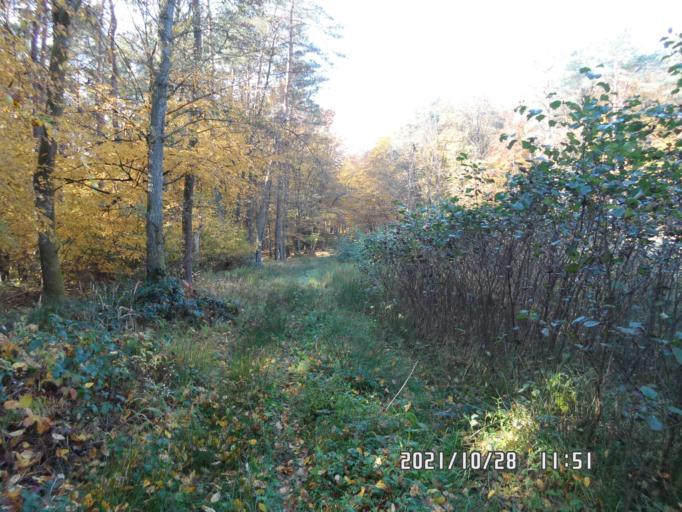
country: SI
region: Hodos-Hodos
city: Hodos
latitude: 46.7796
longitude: 16.3498
